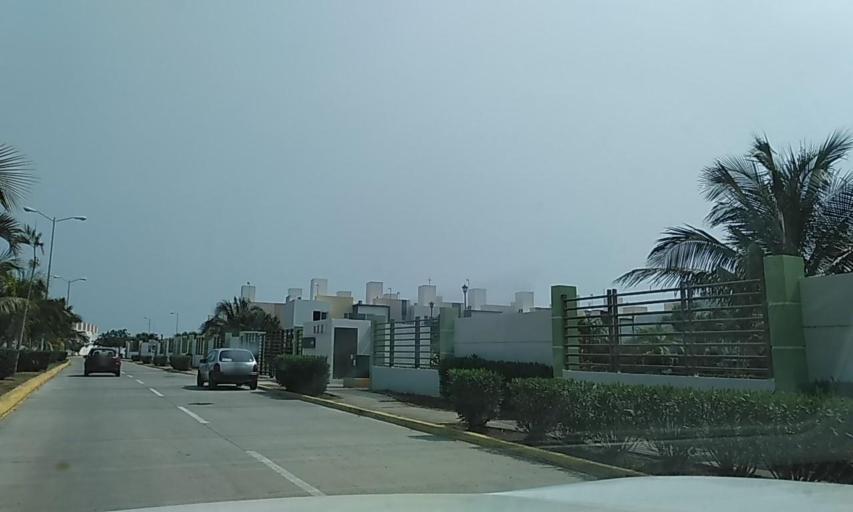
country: MX
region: Veracruz
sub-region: Veracruz
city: Hacienda Sotavento
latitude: 19.1313
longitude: -96.1673
